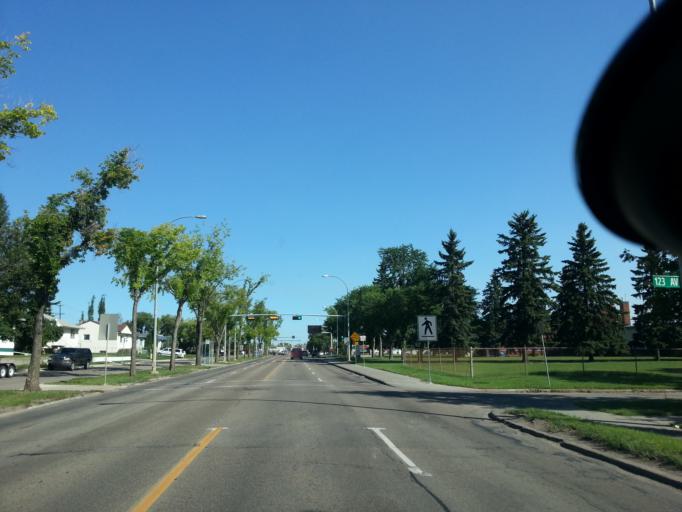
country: CA
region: Alberta
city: Edmonton
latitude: 53.5775
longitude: -113.5412
